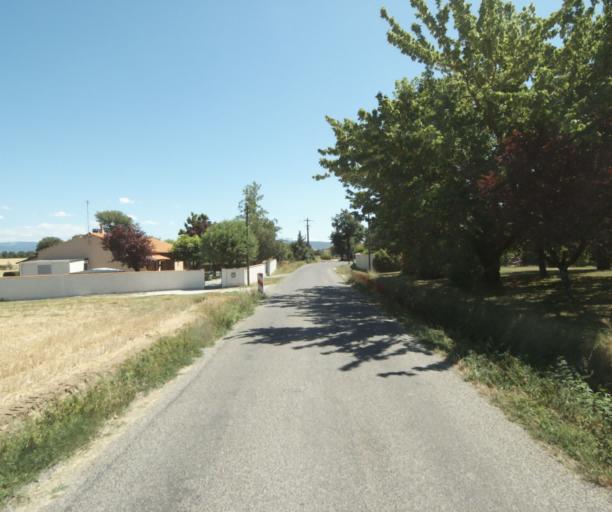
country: FR
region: Midi-Pyrenees
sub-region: Departement de la Haute-Garonne
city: Saint-Felix-Lauragais
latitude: 43.4734
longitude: 1.9299
